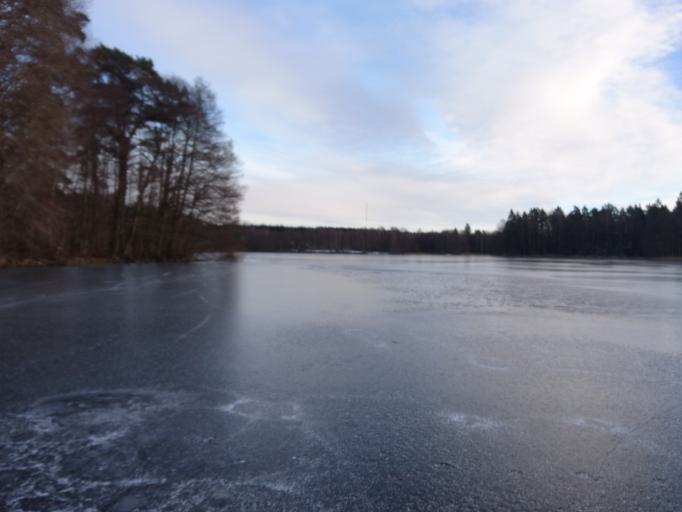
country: SE
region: Blekinge
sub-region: Karlshamns Kommun
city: Karlshamn
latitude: 56.2365
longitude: 14.9695
